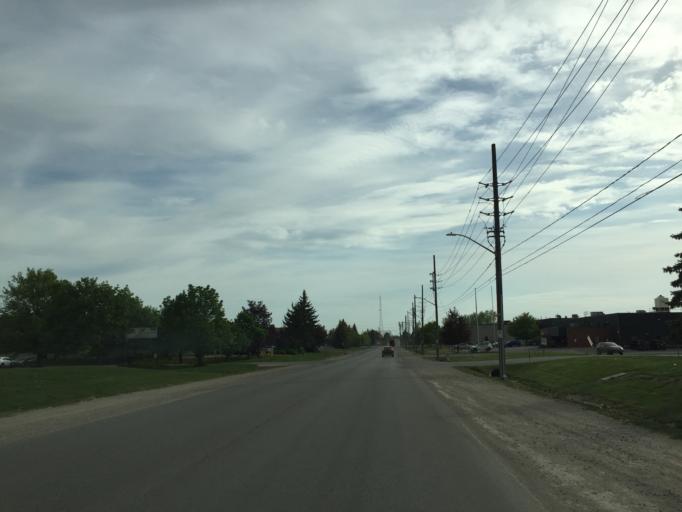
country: CA
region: Ontario
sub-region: Wellington County
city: Guelph
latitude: 43.5373
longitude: -80.3067
